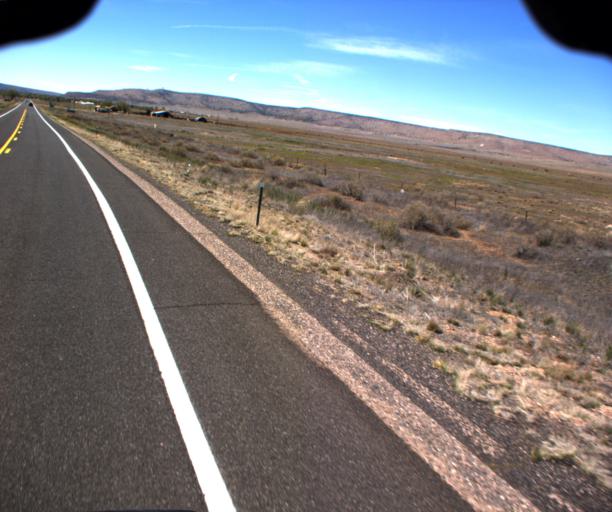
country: US
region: Arizona
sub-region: Yavapai County
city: Paulden
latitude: 35.3231
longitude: -112.8515
